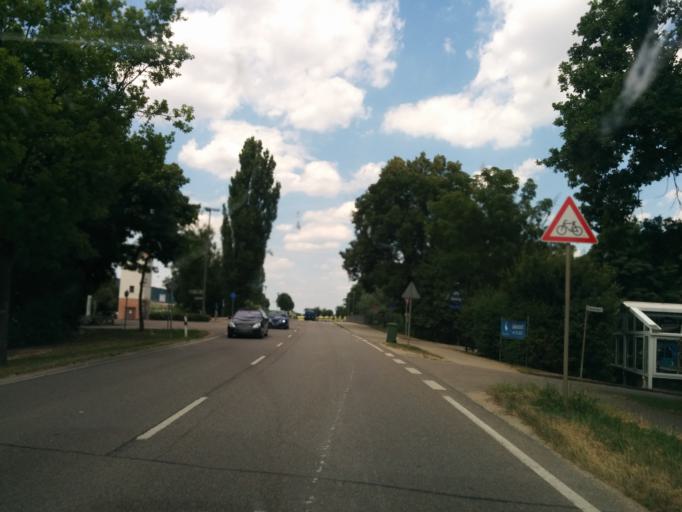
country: DE
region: Bavaria
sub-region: Regierungsbezirk Mittelfranken
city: Treuchtlingen
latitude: 48.9428
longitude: 10.9327
